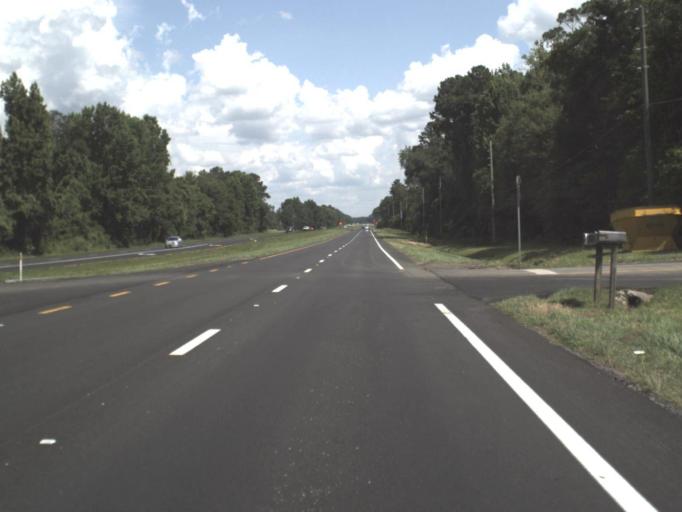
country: US
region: Florida
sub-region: Alachua County
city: Alachua
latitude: 29.7562
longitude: -82.3996
